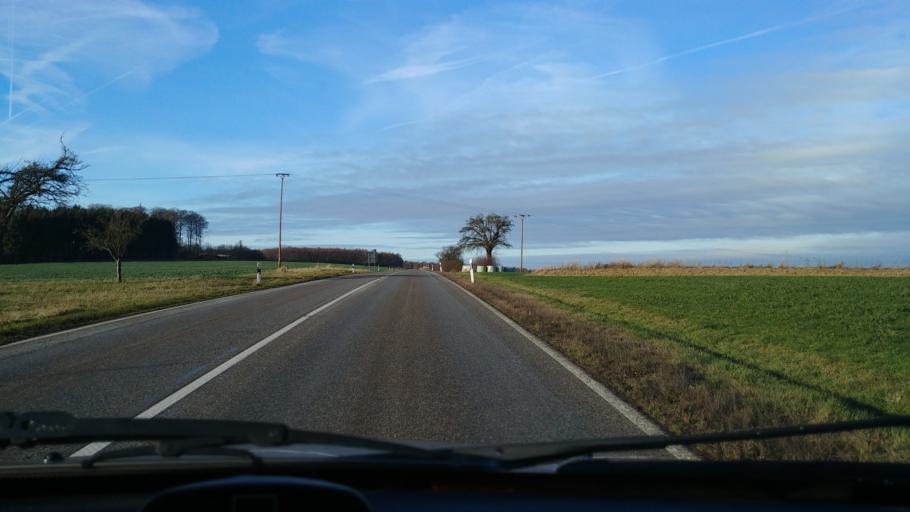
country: DE
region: Rheinland-Pfalz
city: Pohl
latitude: 50.2516
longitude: 7.8646
